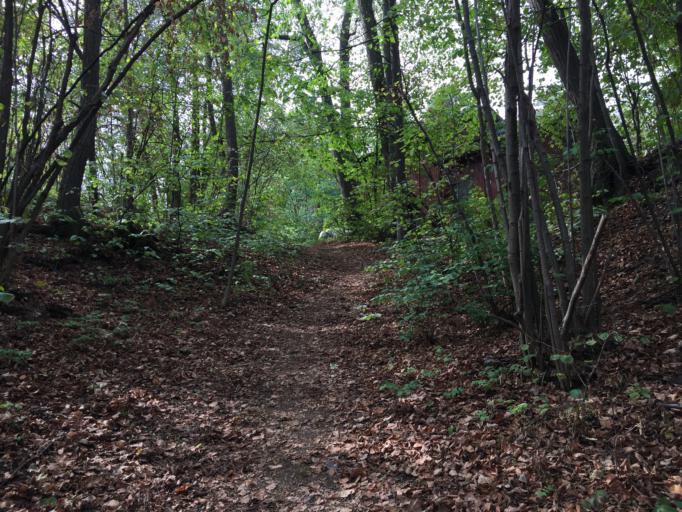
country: NO
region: Oslo
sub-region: Oslo
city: Sjolyststranda
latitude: 59.9175
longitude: 10.6863
